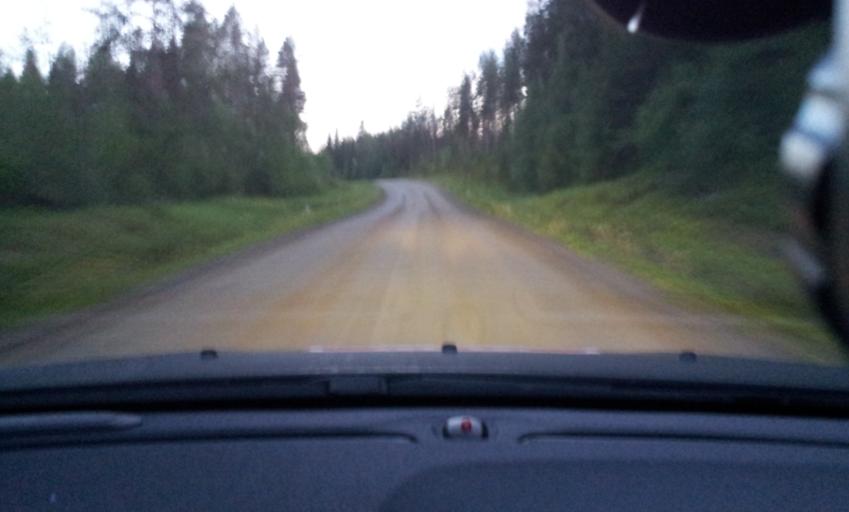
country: SE
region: Vaesternorrland
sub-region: Ange Kommun
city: Ange
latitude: 62.7707
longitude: 15.8890
